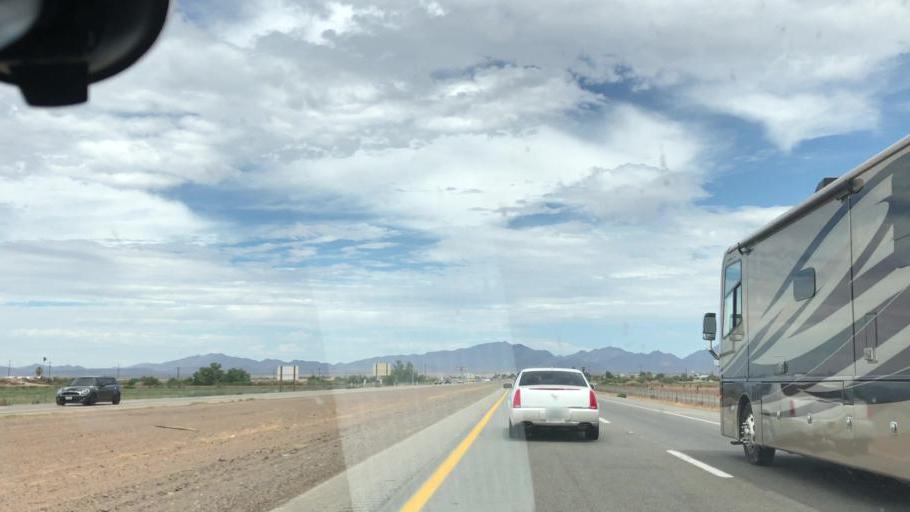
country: US
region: Arizona
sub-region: La Paz County
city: Ehrenberg
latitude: 33.6074
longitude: -114.5568
